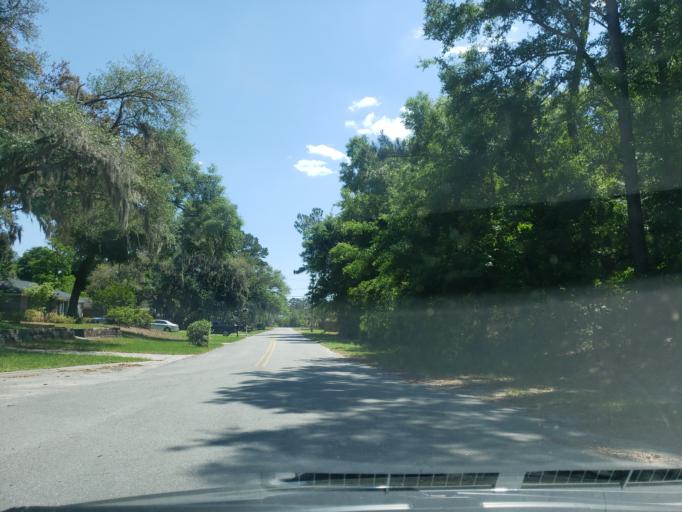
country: US
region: Georgia
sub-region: Chatham County
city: Whitemarsh Island
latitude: 32.0521
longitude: -81.0181
